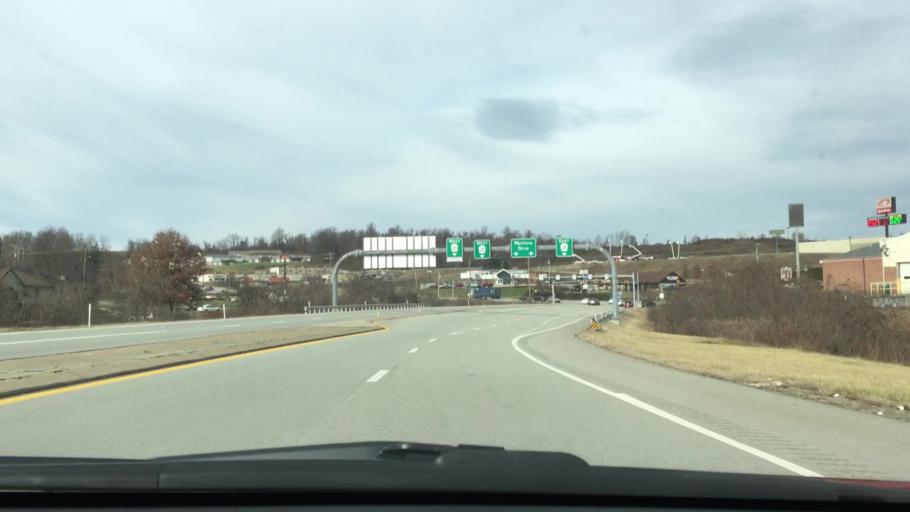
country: US
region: Pennsylvania
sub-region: Fayette County
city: South Uniontown
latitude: 39.9006
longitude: -79.7527
